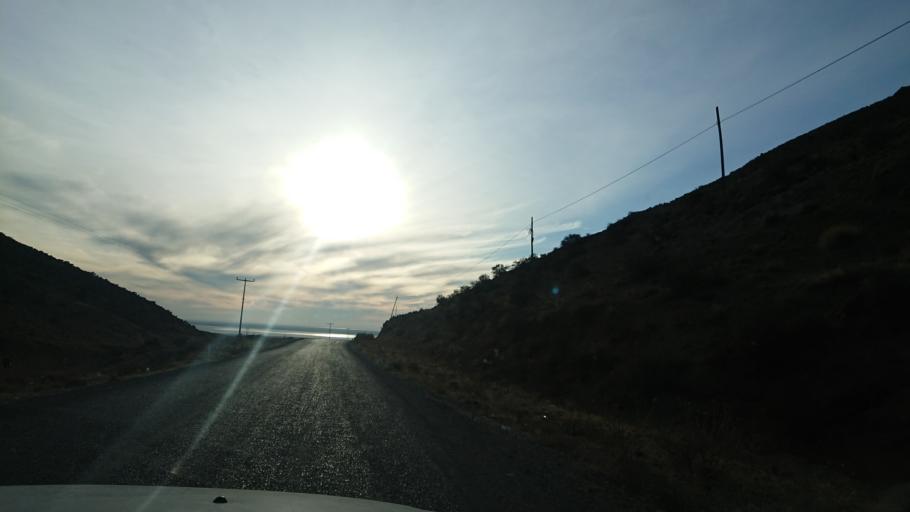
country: TR
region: Ankara
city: Sereflikochisar
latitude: 38.7485
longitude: 33.6866
